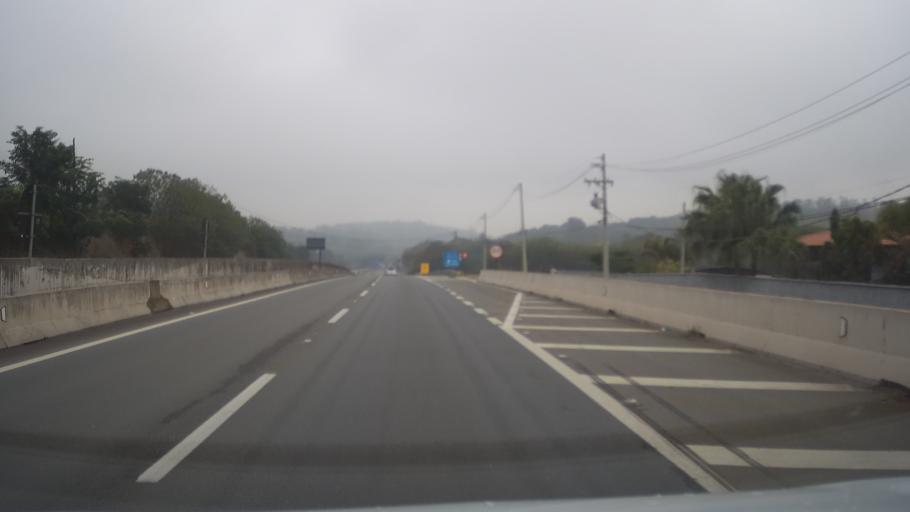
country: BR
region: Sao Paulo
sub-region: Itatiba
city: Itatiba
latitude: -23.0904
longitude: -46.8474
